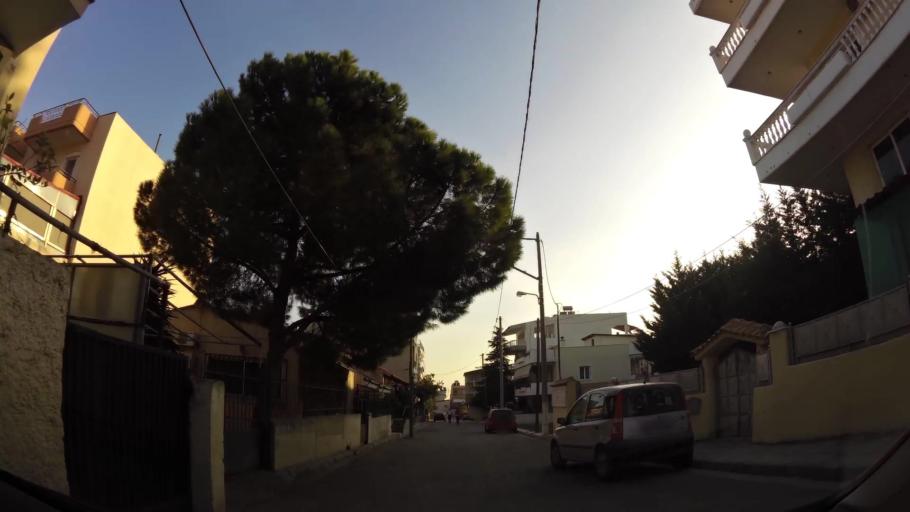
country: GR
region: Attica
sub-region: Nomarchia Anatolikis Attikis
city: Acharnes
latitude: 38.0982
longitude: 23.7402
